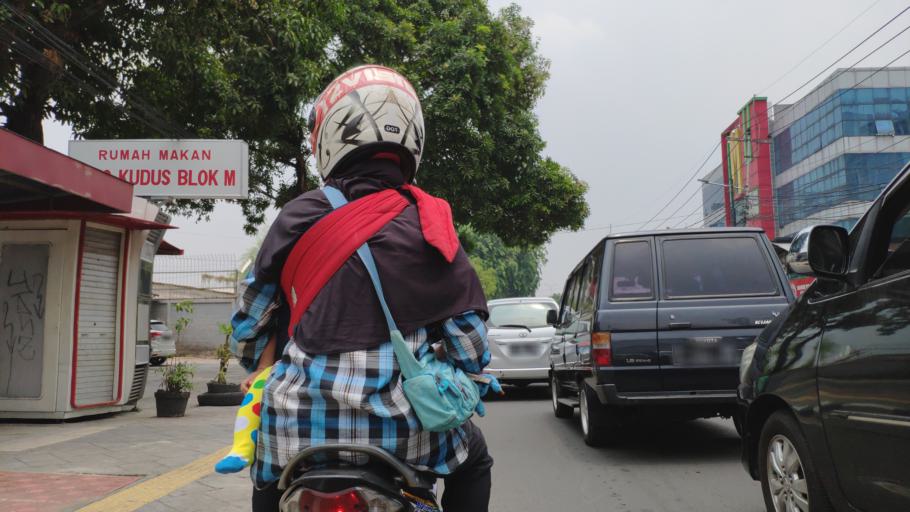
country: ID
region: Banten
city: South Tangerang
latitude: -6.2634
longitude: 106.7663
